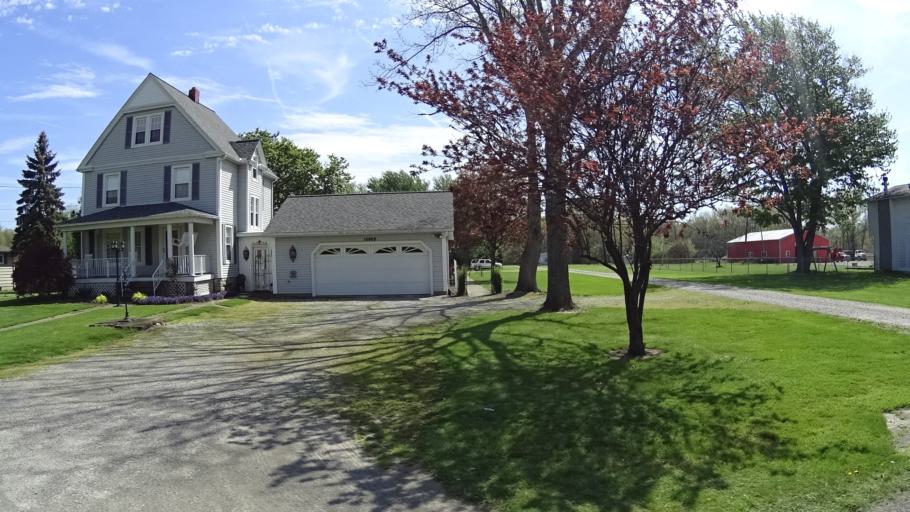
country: US
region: Ohio
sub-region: Lorain County
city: Elyria
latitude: 41.3290
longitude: -82.1175
